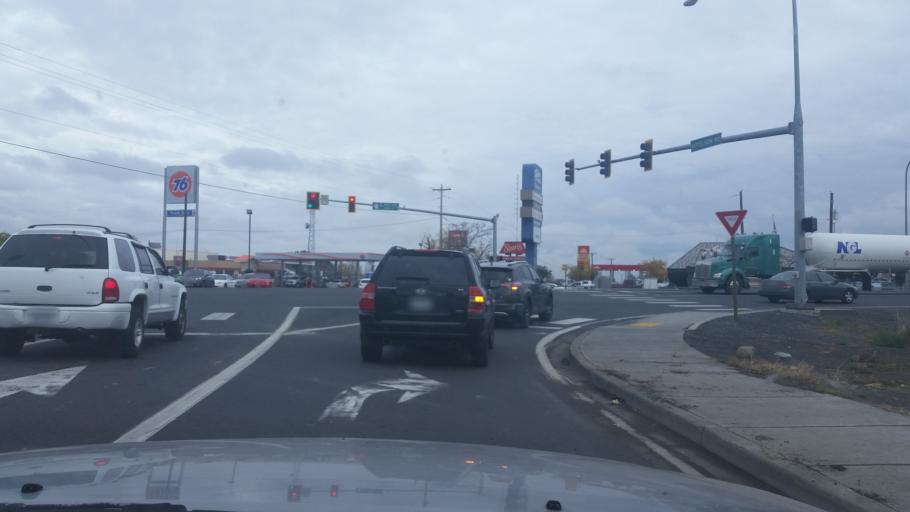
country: US
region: Washington
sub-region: Grant County
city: Moses Lake
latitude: 47.1013
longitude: -119.2468
